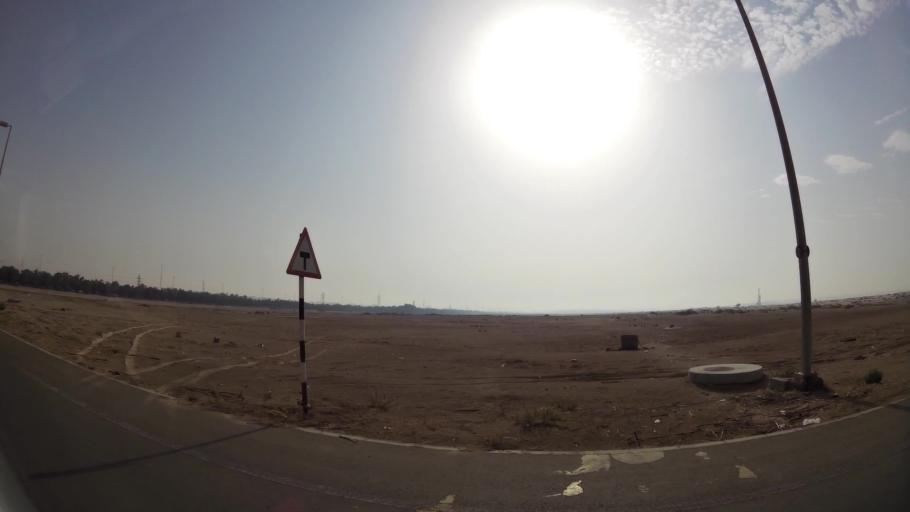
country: AE
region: Abu Dhabi
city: Abu Dhabi
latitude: 24.2625
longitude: 54.6745
